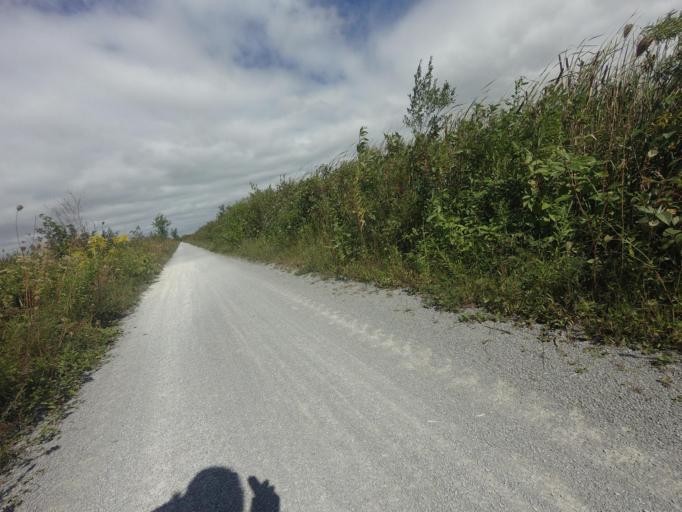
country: CA
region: Ontario
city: Uxbridge
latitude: 44.1890
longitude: -79.0665
